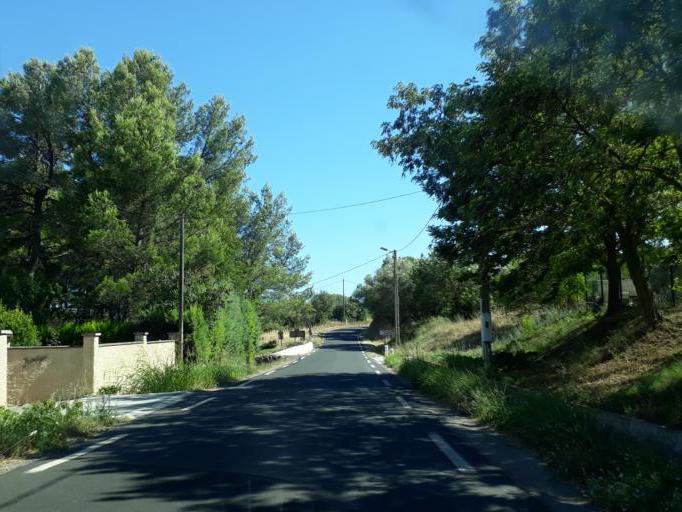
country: FR
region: Languedoc-Roussillon
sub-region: Departement de l'Herault
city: Castelnau-de-Guers
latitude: 43.4321
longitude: 3.4374
